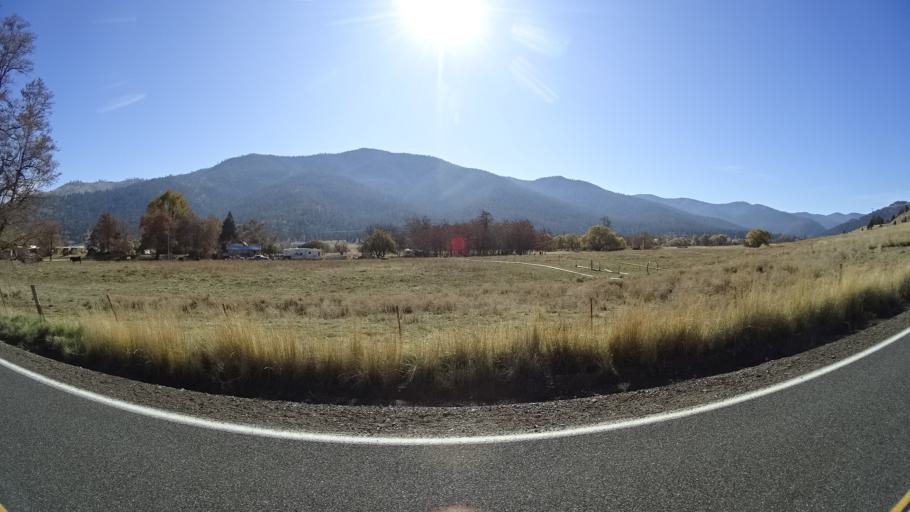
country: US
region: California
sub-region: Siskiyou County
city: Weed
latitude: 41.4939
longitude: -122.5537
